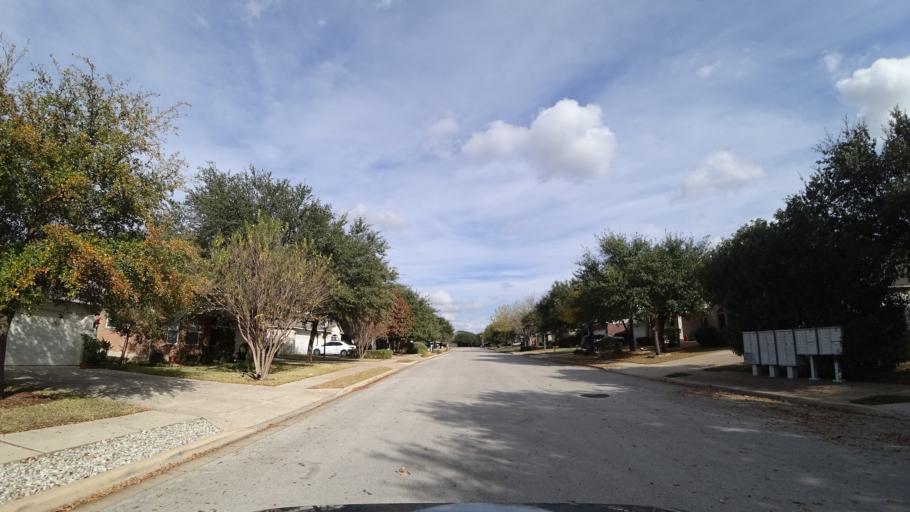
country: US
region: Texas
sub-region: Williamson County
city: Brushy Creek
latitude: 30.5056
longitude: -97.7465
